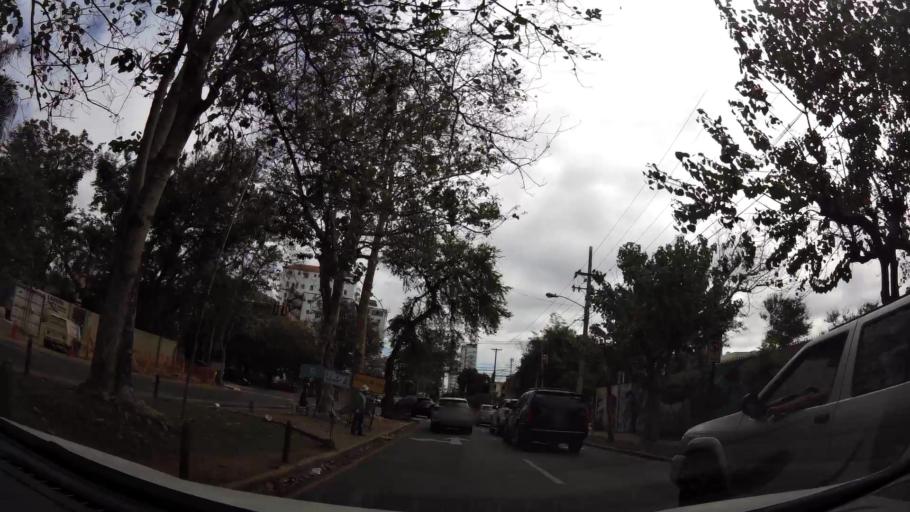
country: DO
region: Nacional
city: Bella Vista
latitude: 18.4489
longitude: -69.9518
